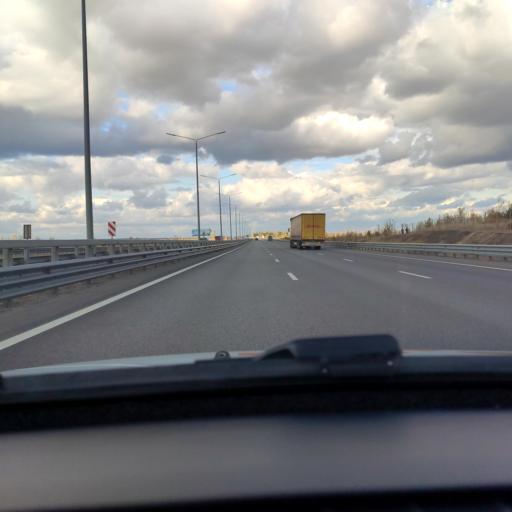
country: RU
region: Voronezj
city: Somovo
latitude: 51.7508
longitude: 39.3057
